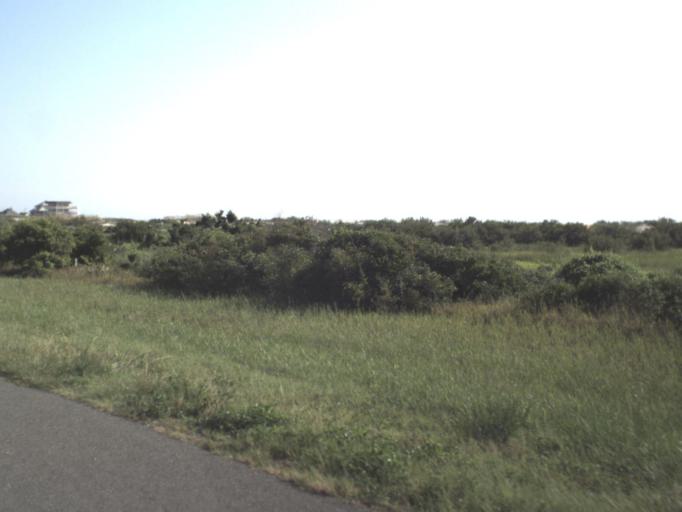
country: US
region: Florida
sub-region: Flagler County
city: Palm Coast
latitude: 29.6913
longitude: -81.2238
